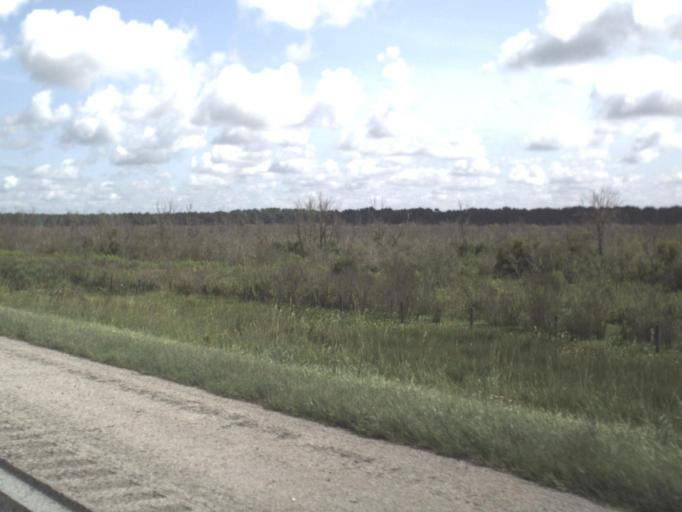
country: US
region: Florida
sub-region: Alachua County
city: Gainesville
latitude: 29.5740
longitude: -82.3532
